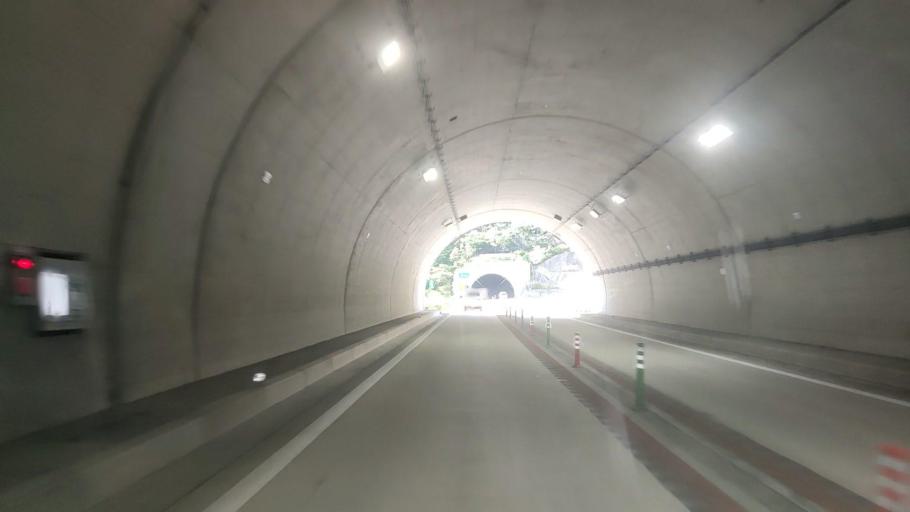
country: JP
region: Wakayama
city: Tanabe
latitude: 33.5981
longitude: 135.4334
